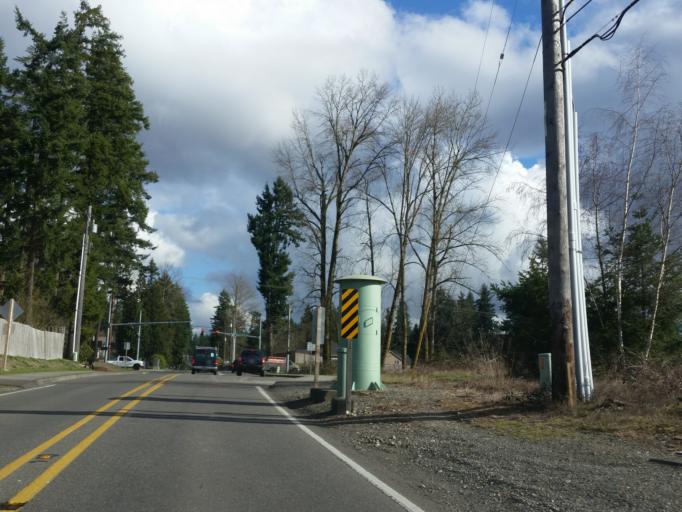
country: US
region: Washington
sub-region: Pierce County
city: South Hill
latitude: 47.1368
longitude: -122.2661
